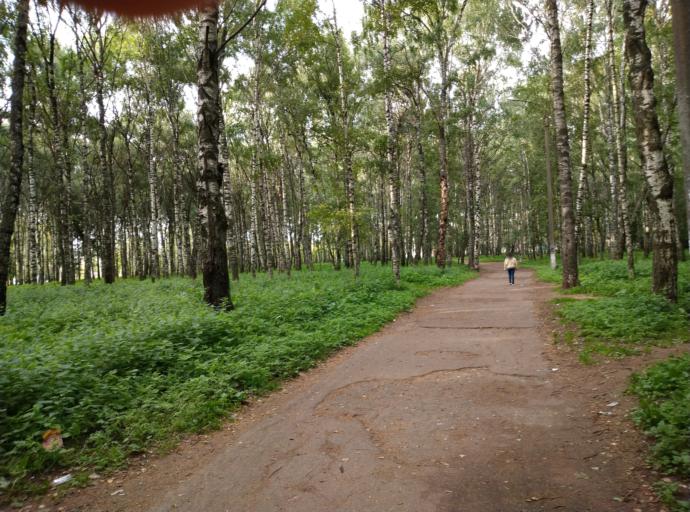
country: RU
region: Kostroma
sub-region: Kostromskoy Rayon
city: Kostroma
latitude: 57.7608
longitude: 40.9634
